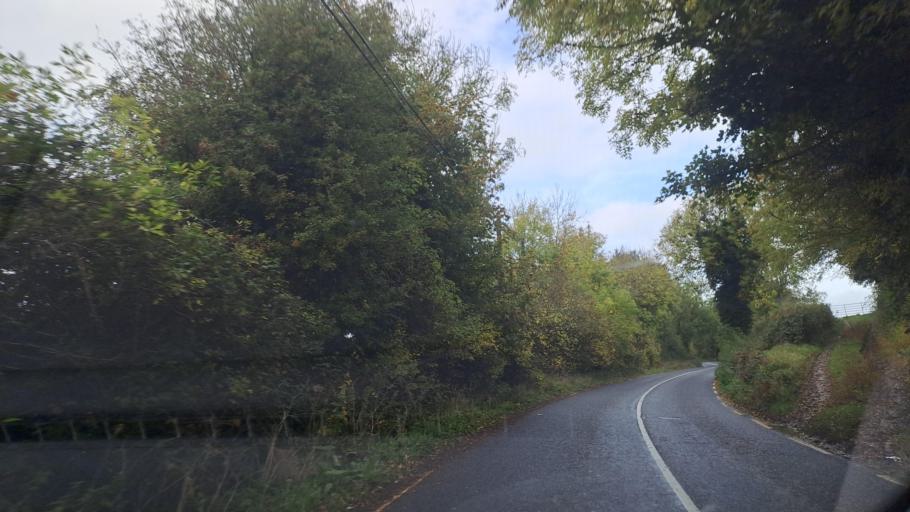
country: IE
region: Ulster
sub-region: County Monaghan
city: Carrickmacross
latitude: 53.9257
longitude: -6.7155
